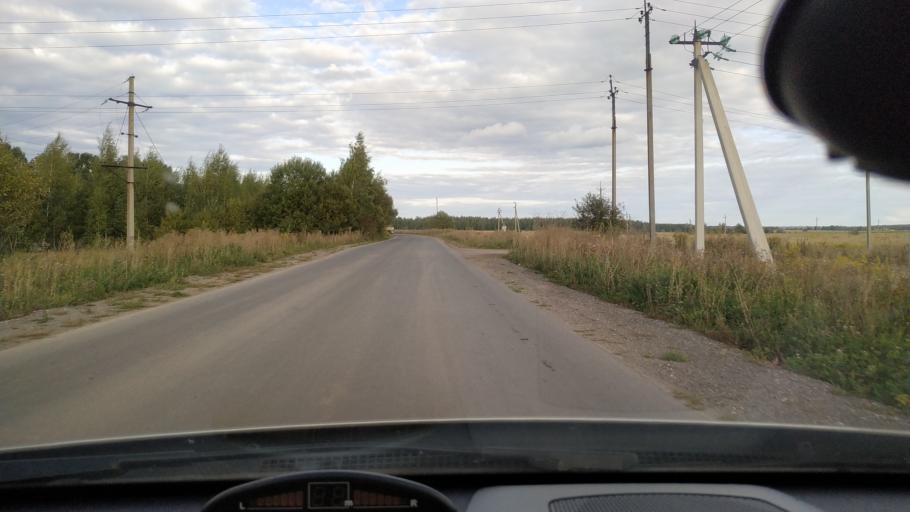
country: RU
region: Rjazan
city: Polyany
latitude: 54.5766
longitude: 39.8509
